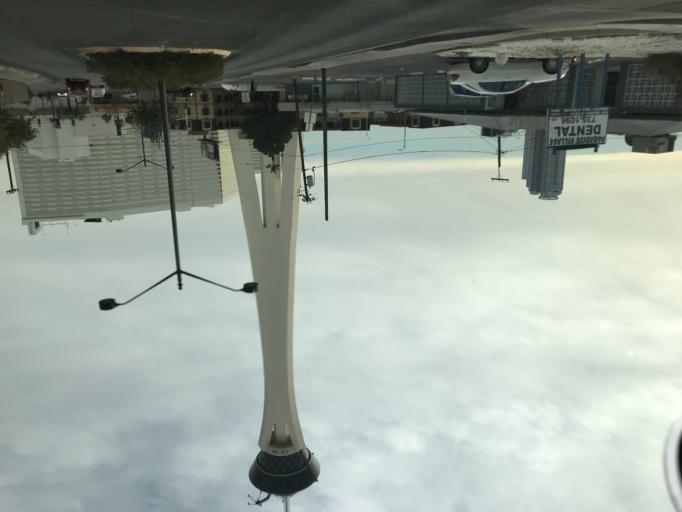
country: US
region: Nevada
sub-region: Clark County
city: Las Vegas
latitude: 36.1476
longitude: -115.1517
